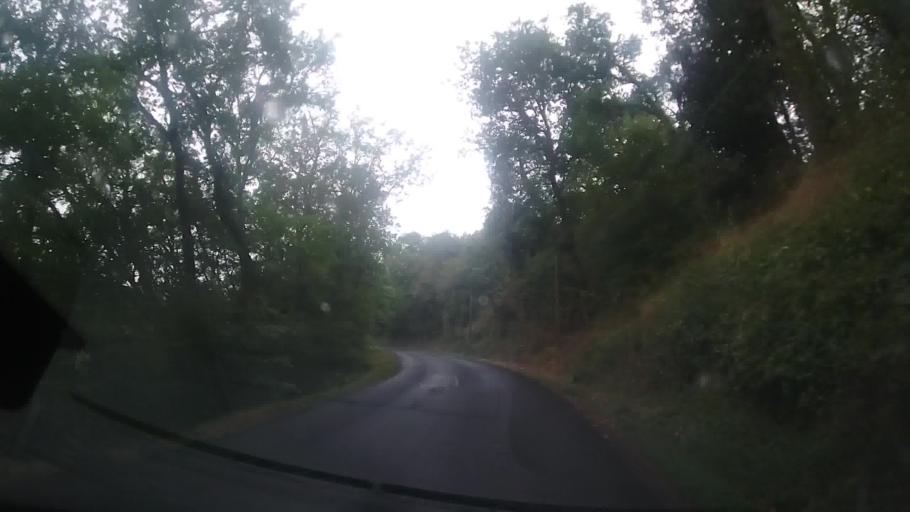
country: FR
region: Aquitaine
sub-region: Departement de la Dordogne
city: Cenac-et-Saint-Julien
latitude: 44.7898
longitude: 1.1877
